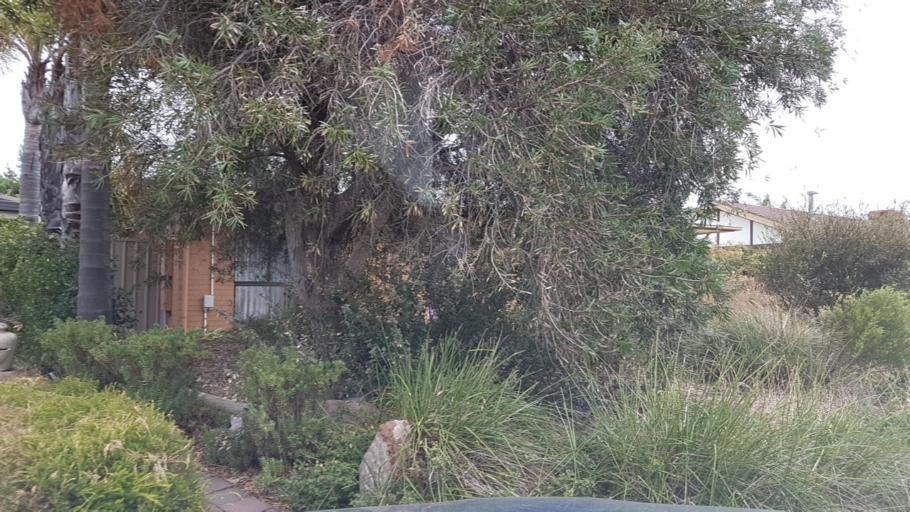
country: AU
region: South Australia
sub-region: Onkaparinga
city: Moana
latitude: -35.1945
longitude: 138.4784
